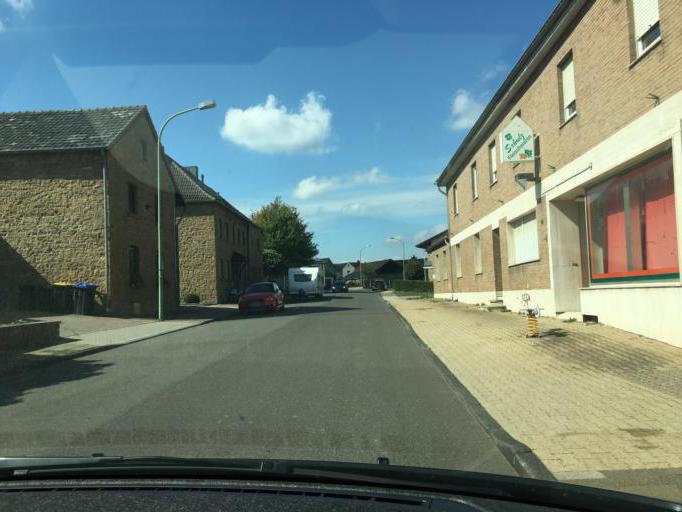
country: DE
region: North Rhine-Westphalia
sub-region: Regierungsbezirk Koln
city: Nideggen
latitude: 50.6802
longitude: 6.5244
